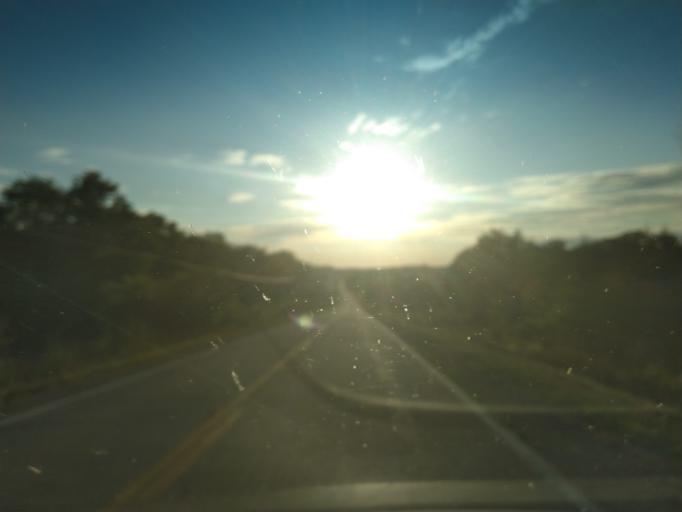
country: US
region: Iowa
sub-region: Jackson County
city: Maquoketa
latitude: 42.1643
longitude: -90.7066
